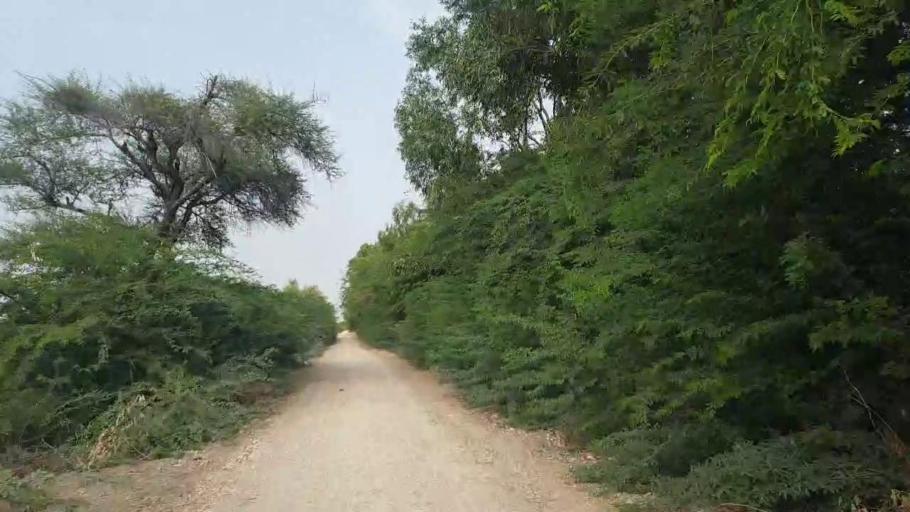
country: PK
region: Sindh
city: Badin
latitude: 24.5988
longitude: 68.7413
